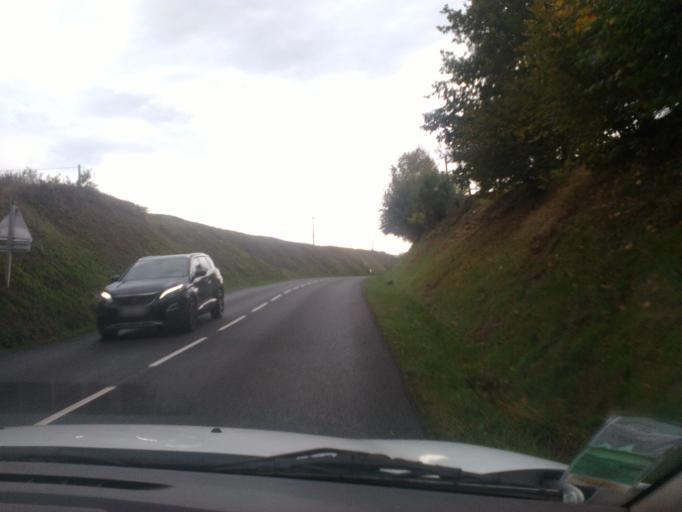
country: FR
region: Lorraine
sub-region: Departement des Vosges
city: Granges-sur-Vologne
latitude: 48.1810
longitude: 6.8100
